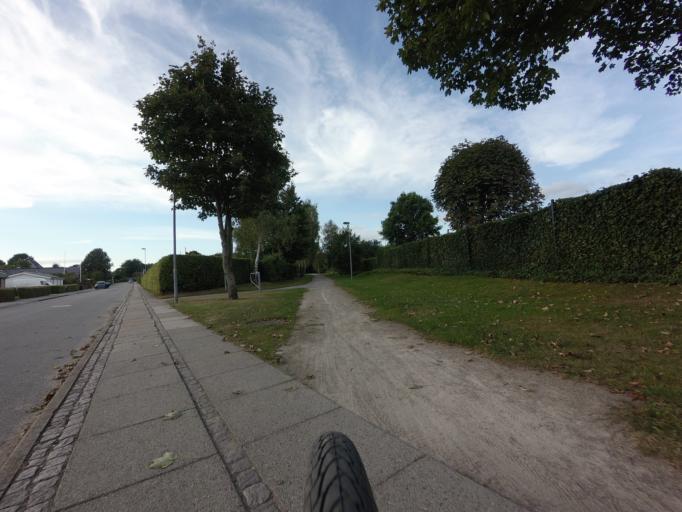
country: DK
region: Central Jutland
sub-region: Ikast-Brande Kommune
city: Brande
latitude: 55.9373
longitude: 9.1420
